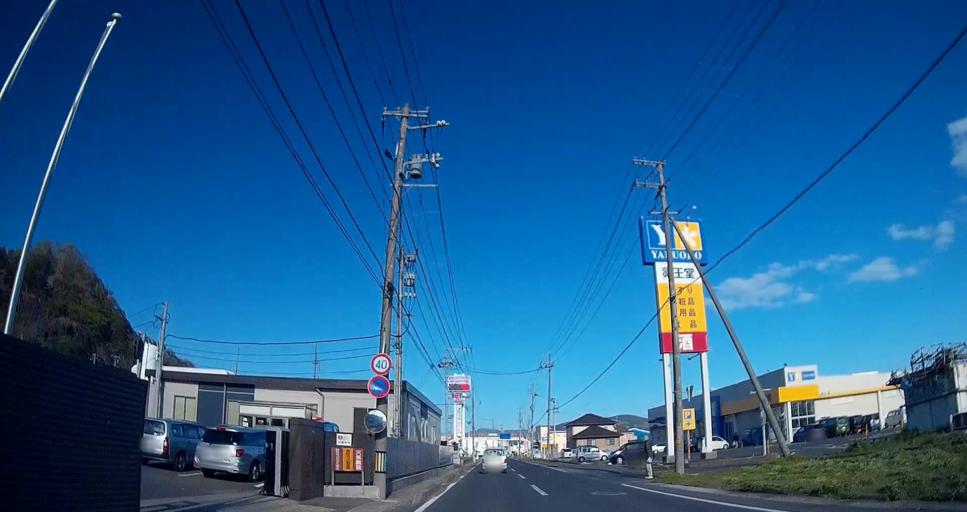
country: JP
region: Miyagi
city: Ishinomaki
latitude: 38.4197
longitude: 141.3315
